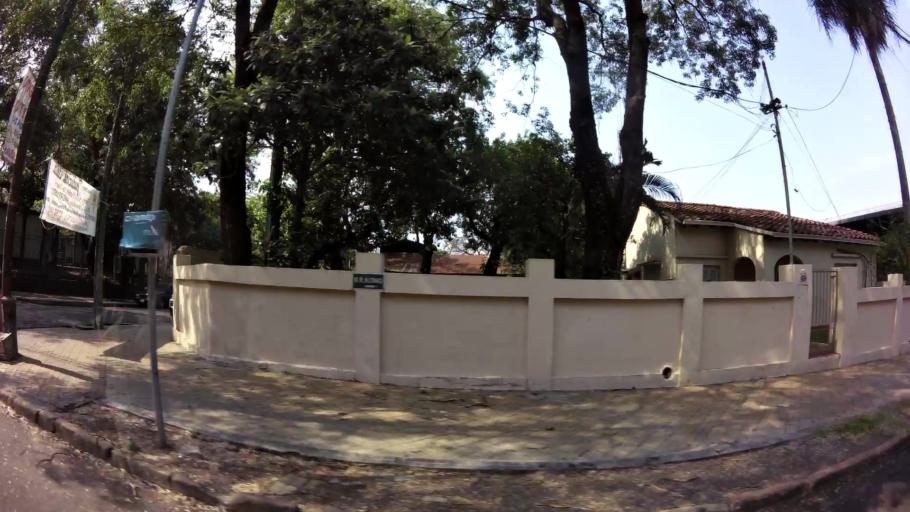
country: PY
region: Asuncion
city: Asuncion
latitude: -25.2878
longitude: -57.6553
